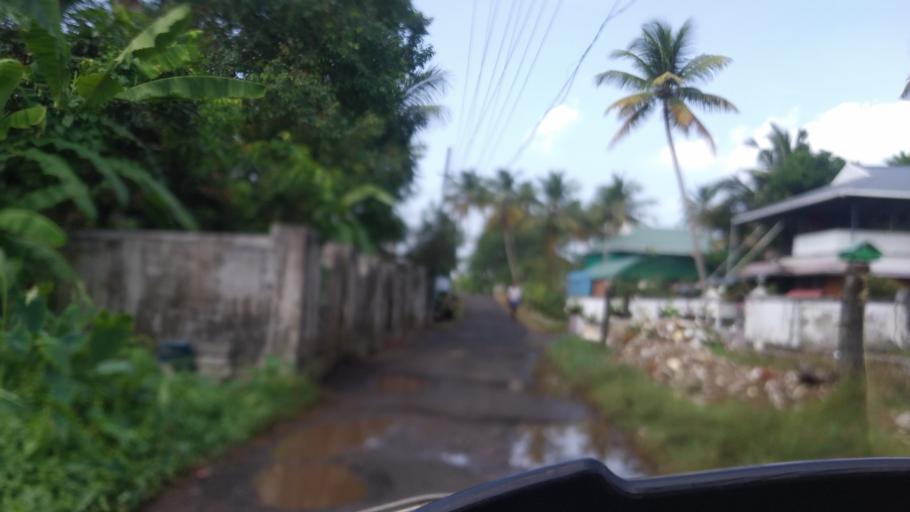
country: IN
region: Kerala
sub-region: Thrissur District
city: Kodungallur
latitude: 10.1372
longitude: 76.2150
